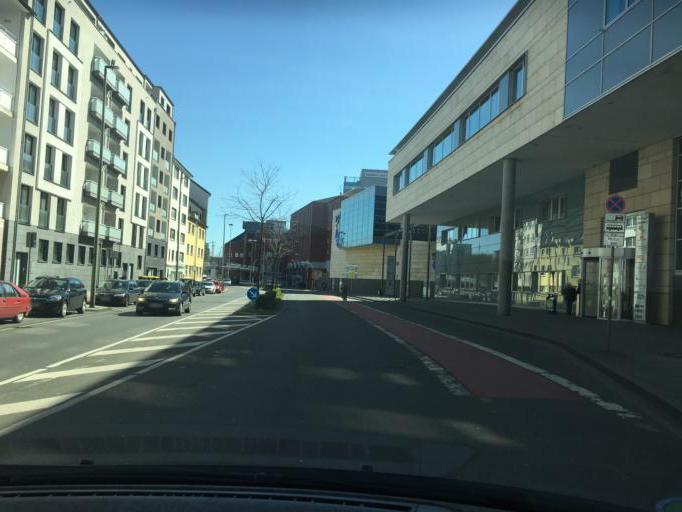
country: DE
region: North Rhine-Westphalia
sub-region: Regierungsbezirk Dusseldorf
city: Duisburg
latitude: 51.4341
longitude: 6.7712
